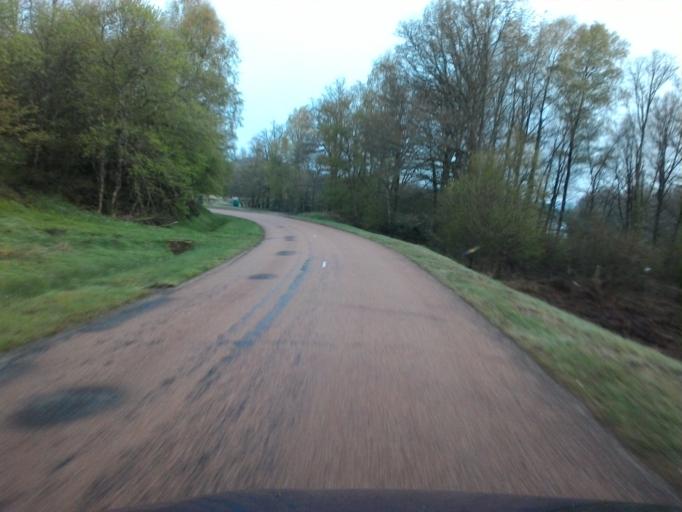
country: FR
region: Bourgogne
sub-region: Departement de la Cote-d'Or
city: Saulieu
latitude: 47.2548
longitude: 4.1933
